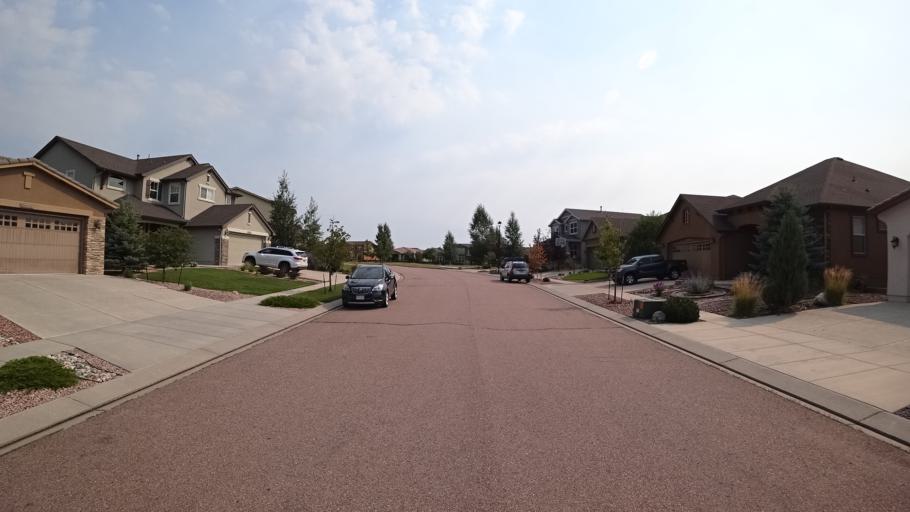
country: US
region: Colorado
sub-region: El Paso County
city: Black Forest
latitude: 38.9647
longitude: -104.7320
